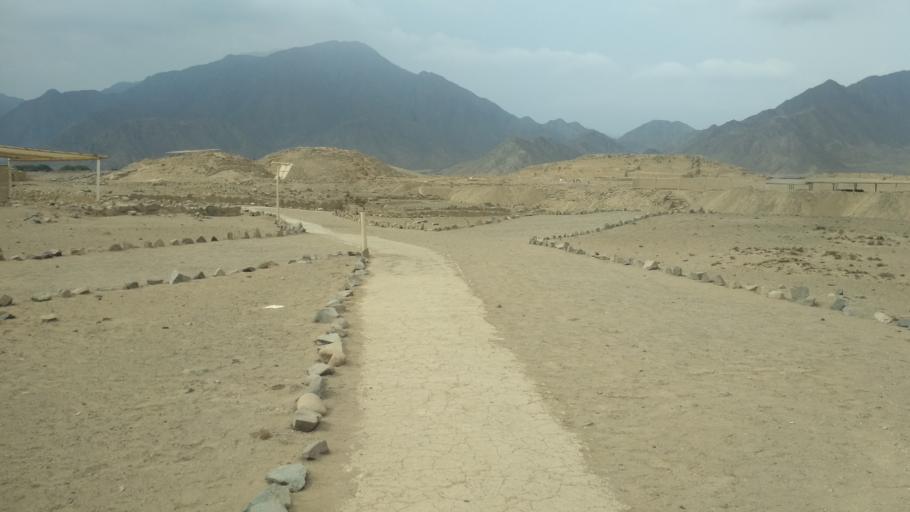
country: PE
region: Lima
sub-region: Huaura
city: Vegueta
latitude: -10.8952
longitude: -77.5221
